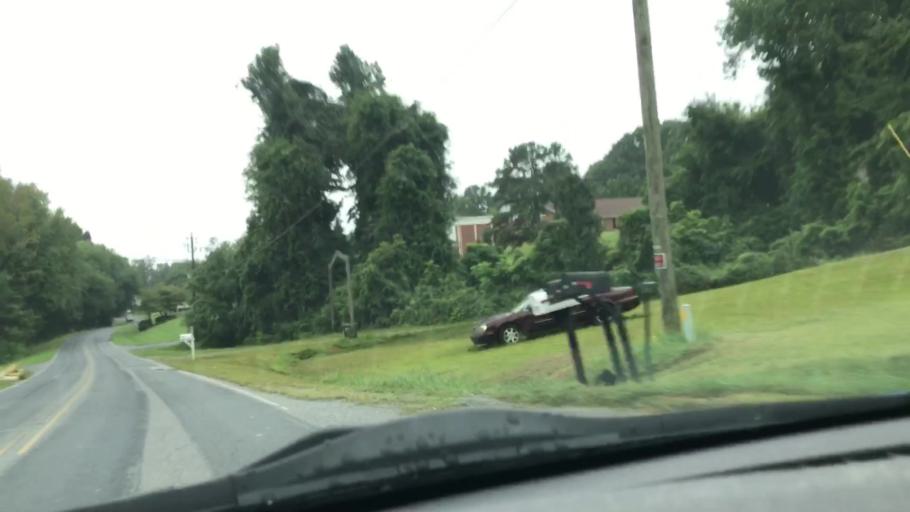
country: US
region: North Carolina
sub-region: Randolph County
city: Asheboro
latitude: 35.7227
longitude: -79.8015
